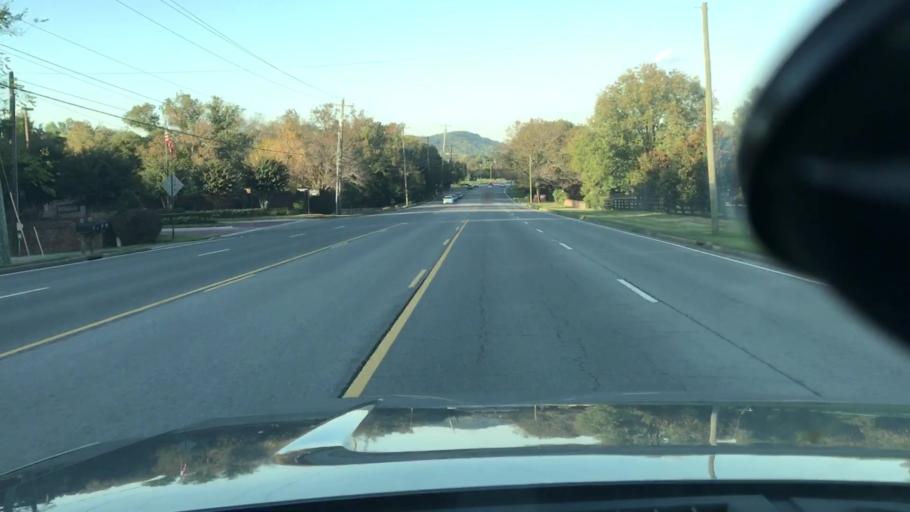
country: US
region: Tennessee
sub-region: Williamson County
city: Brentwood Estates
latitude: 36.0032
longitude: -86.8071
